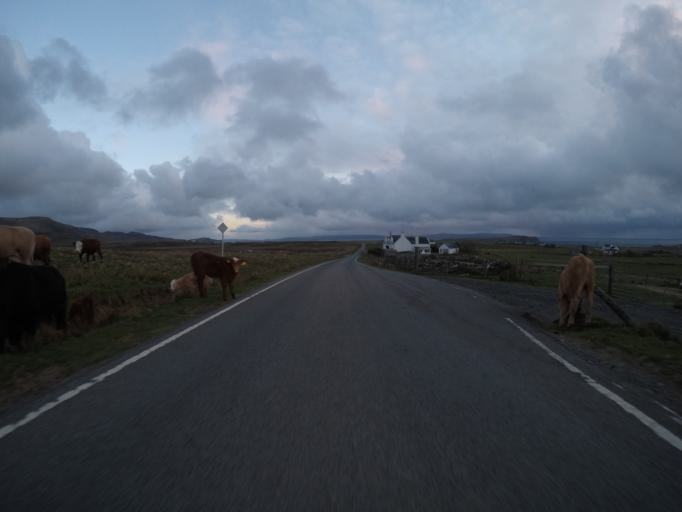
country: GB
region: Scotland
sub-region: Highland
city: Portree
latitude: 57.6582
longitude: -6.3741
